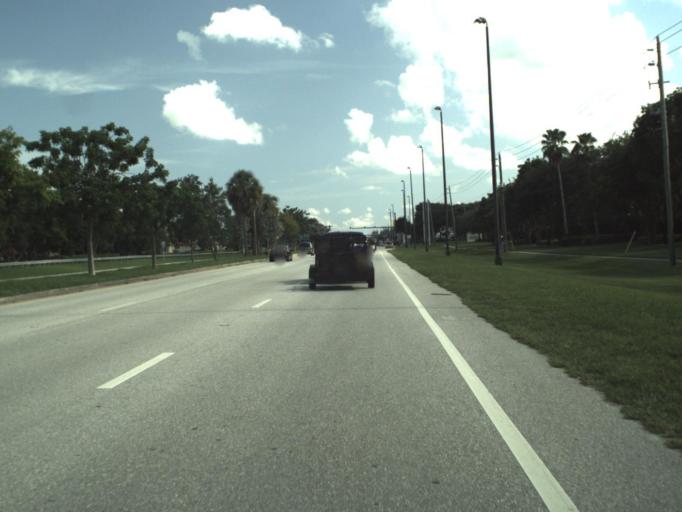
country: US
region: Florida
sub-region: Palm Beach County
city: Boca Pointe
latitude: 26.3422
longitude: -80.2033
